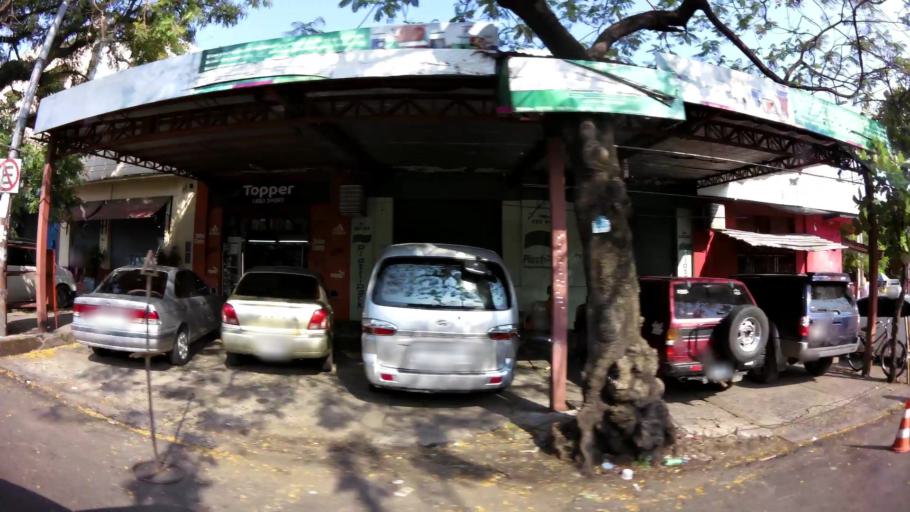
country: PY
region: Asuncion
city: Asuncion
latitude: -25.2962
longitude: -57.6242
